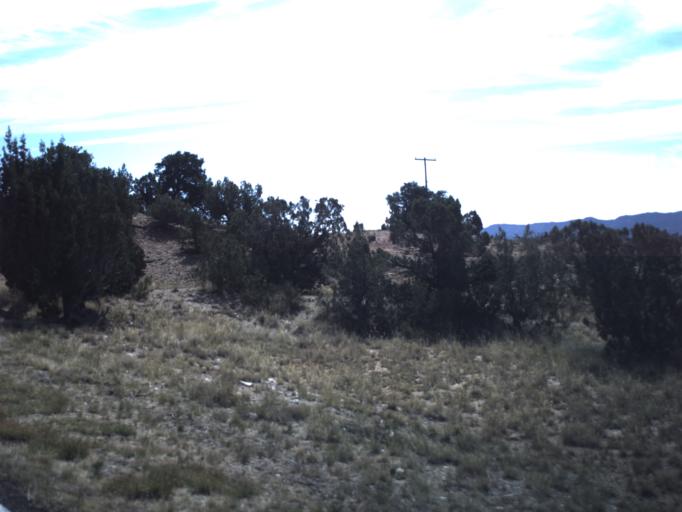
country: US
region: Utah
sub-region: Wayne County
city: Loa
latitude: 37.7398
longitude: -111.5523
